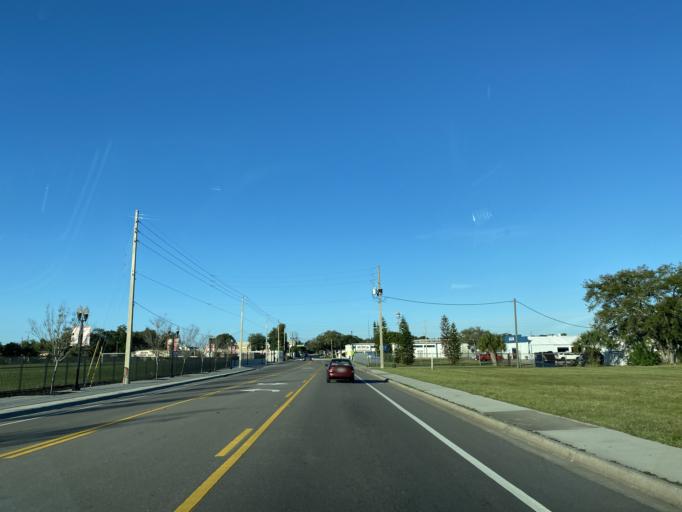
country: US
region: Florida
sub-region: Orange County
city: Orlando
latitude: 28.5494
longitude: -81.3913
